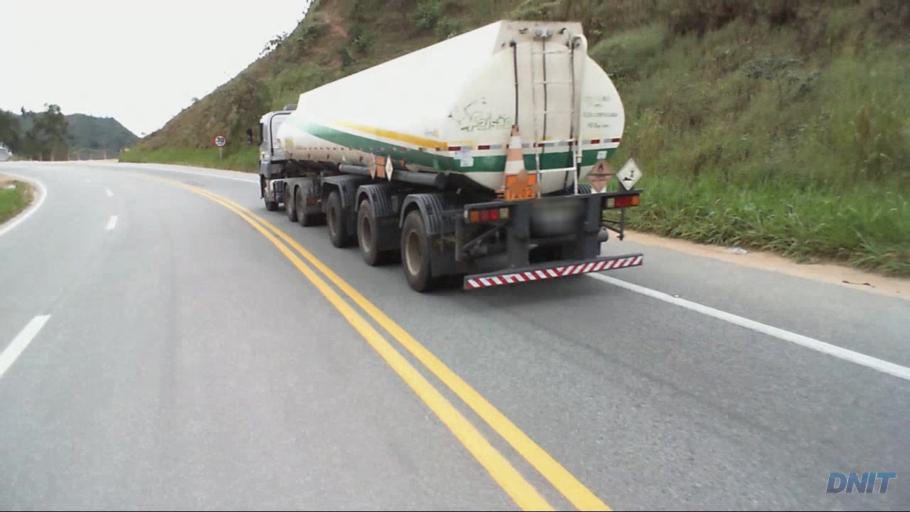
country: BR
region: Minas Gerais
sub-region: Nova Era
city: Nova Era
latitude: -19.6401
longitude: -42.8996
